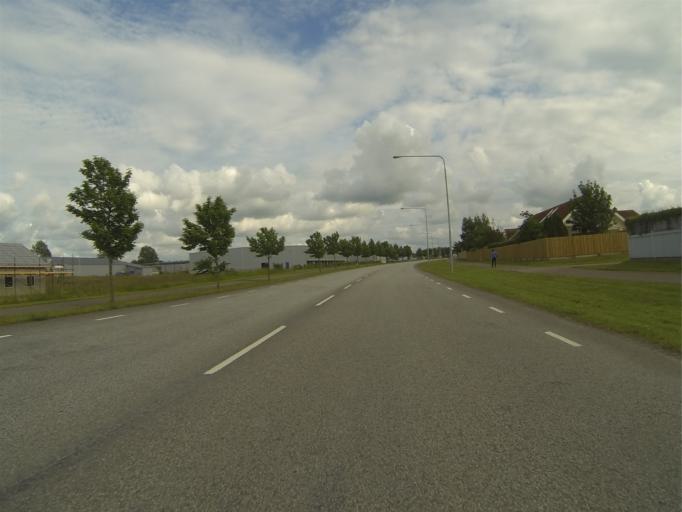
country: SE
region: Skane
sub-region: Staffanstorps Kommun
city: Staffanstorp
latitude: 55.6446
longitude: 13.2274
